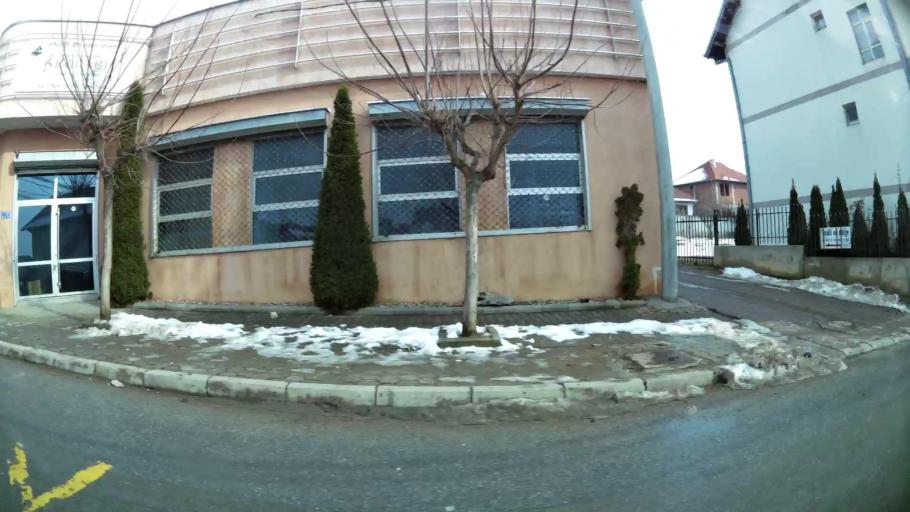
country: XK
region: Pristina
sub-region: Komuna e Prishtines
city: Pristina
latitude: 42.6836
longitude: 21.1641
